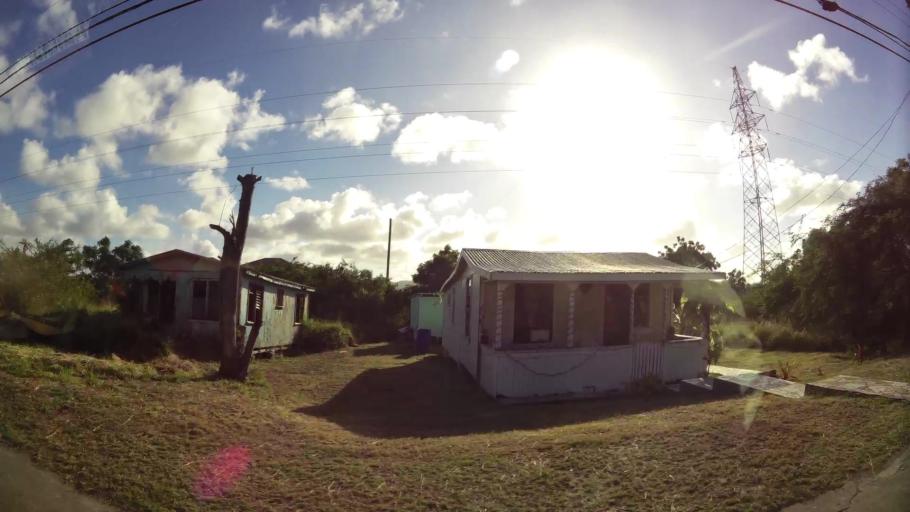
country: AG
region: Saint George
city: Piggotts
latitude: 17.1207
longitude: -61.8013
